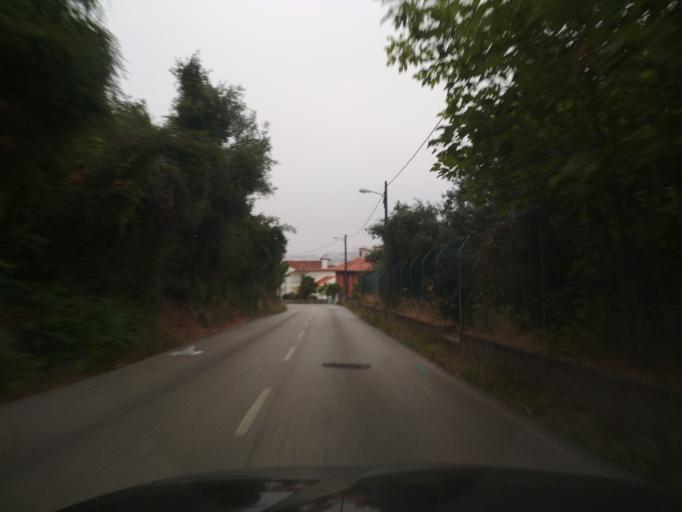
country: PT
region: Coimbra
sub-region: Coimbra
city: Coimbra
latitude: 40.1943
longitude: -8.4366
